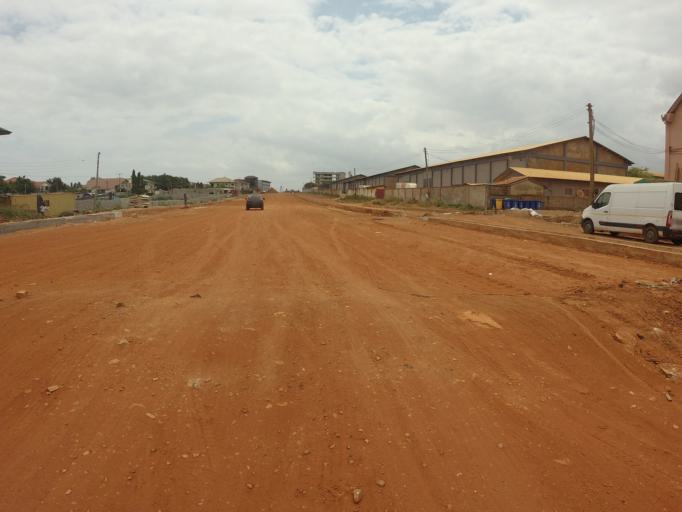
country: GH
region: Greater Accra
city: Medina Estates
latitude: 5.6267
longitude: -0.1486
